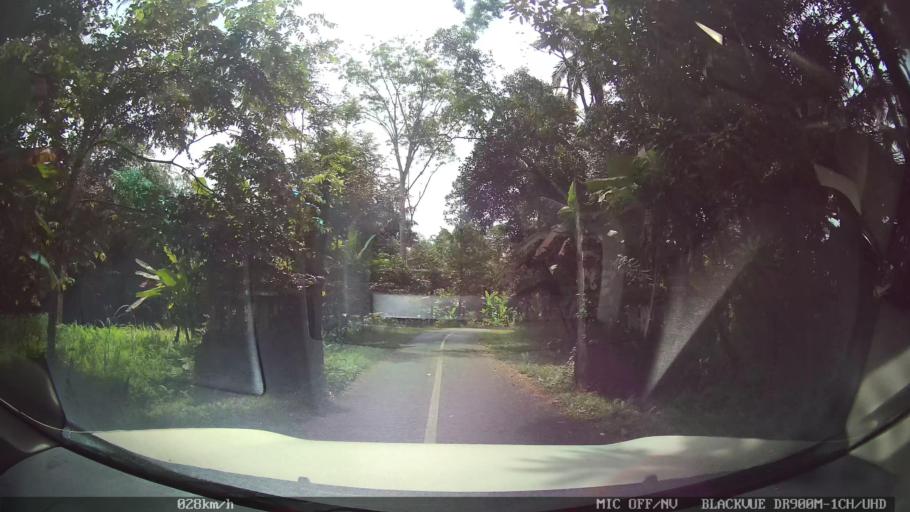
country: ID
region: Bali
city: Bunutan
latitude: -8.4612
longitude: 115.2334
